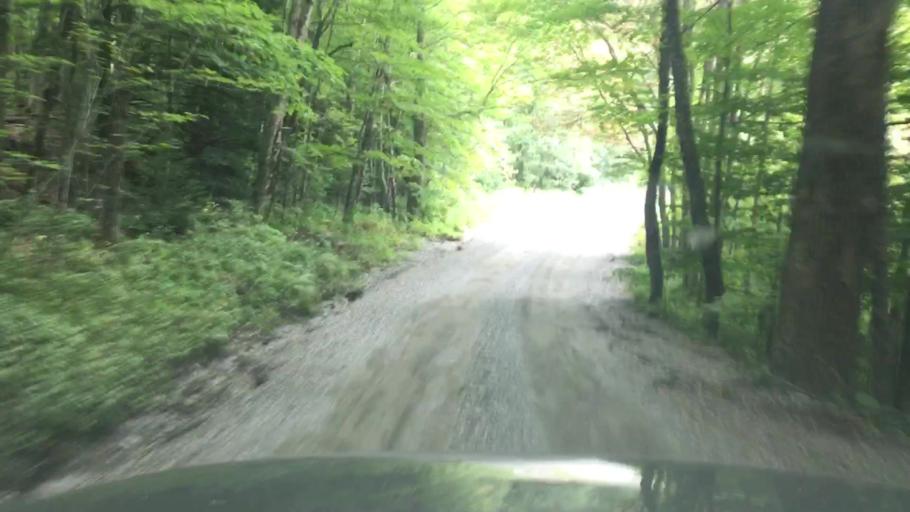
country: US
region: Vermont
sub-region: Windham County
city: Dover
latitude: 42.8366
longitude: -72.7676
